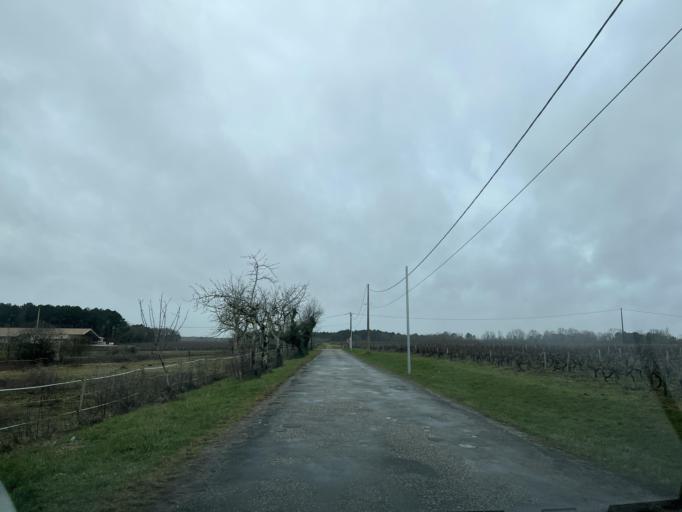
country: FR
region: Aquitaine
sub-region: Departement de la Gironde
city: Gaillan-en-Medoc
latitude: 45.3548
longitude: -0.9832
